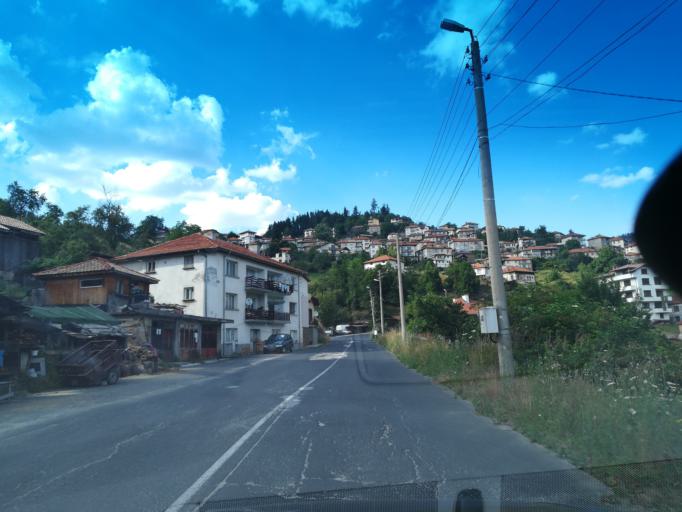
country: BG
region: Smolyan
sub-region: Obshtina Smolyan
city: Smolyan
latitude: 41.6530
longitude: 24.7707
